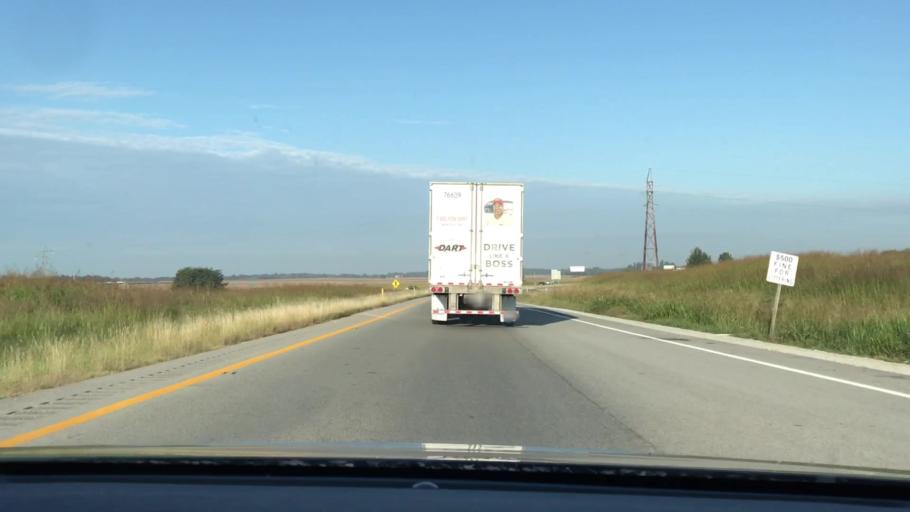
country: US
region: Kentucky
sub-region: Christian County
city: Oak Grove
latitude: 36.6835
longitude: -87.4056
